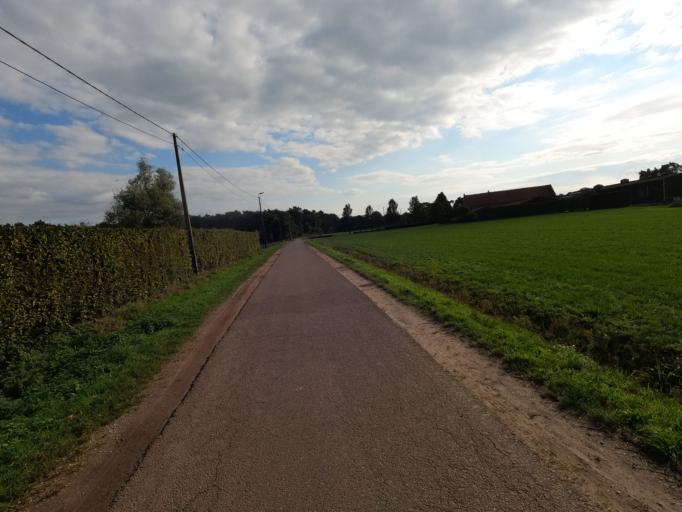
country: BE
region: Flanders
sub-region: Provincie Antwerpen
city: Vorselaar
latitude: 51.1900
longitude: 4.7833
